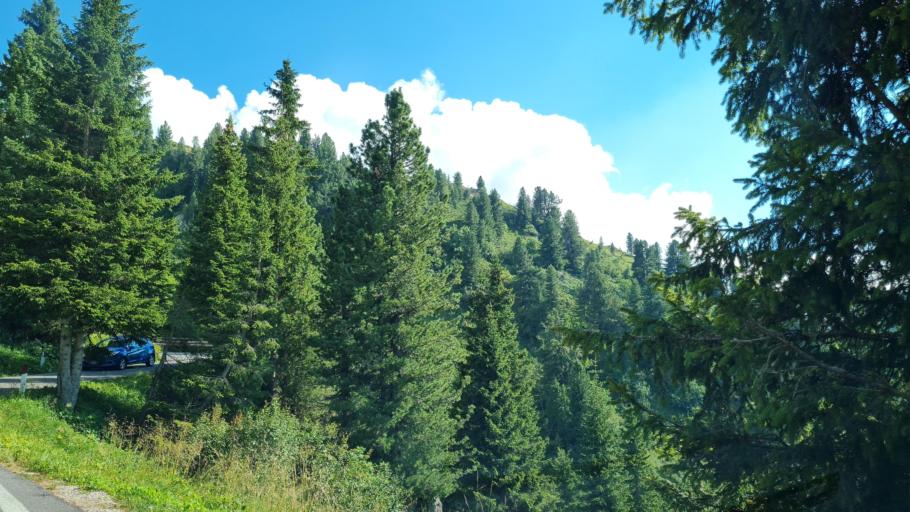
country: IT
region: Trentino-Alto Adige
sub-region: Provincia di Trento
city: Palu del Fersina
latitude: 46.1755
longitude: 11.4380
